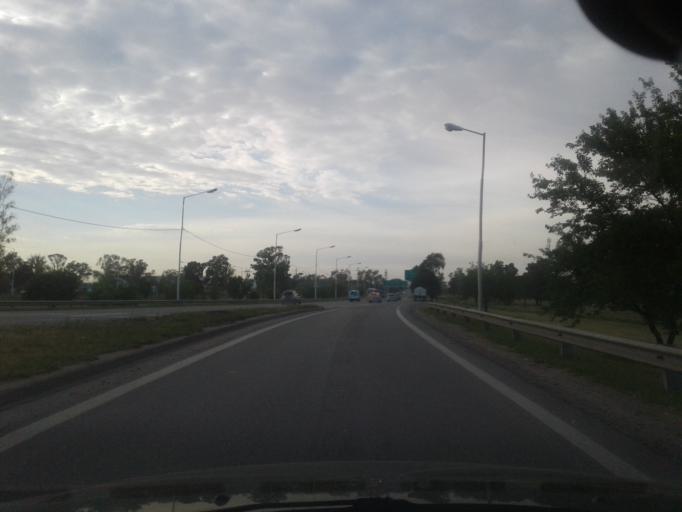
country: AR
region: Santa Fe
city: Granadero Baigorria
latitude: -32.9038
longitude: -60.7252
